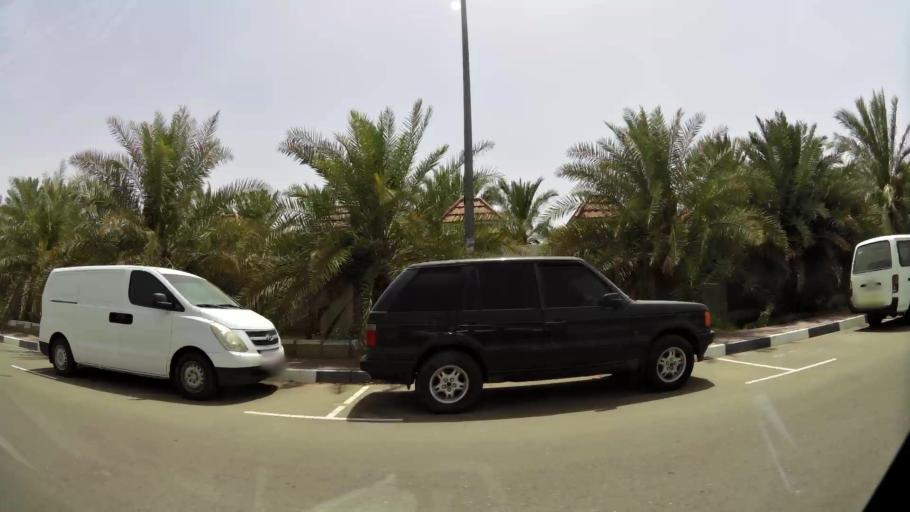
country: AE
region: Abu Dhabi
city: Al Ain
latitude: 24.1905
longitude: 55.6763
